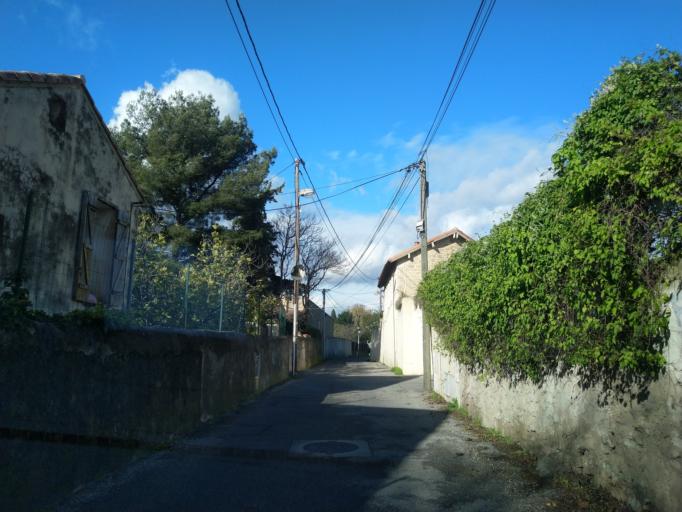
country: FR
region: Provence-Alpes-Cote d'Azur
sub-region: Departement des Bouches-du-Rhone
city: Marseille 12
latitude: 43.3116
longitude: 5.4340
